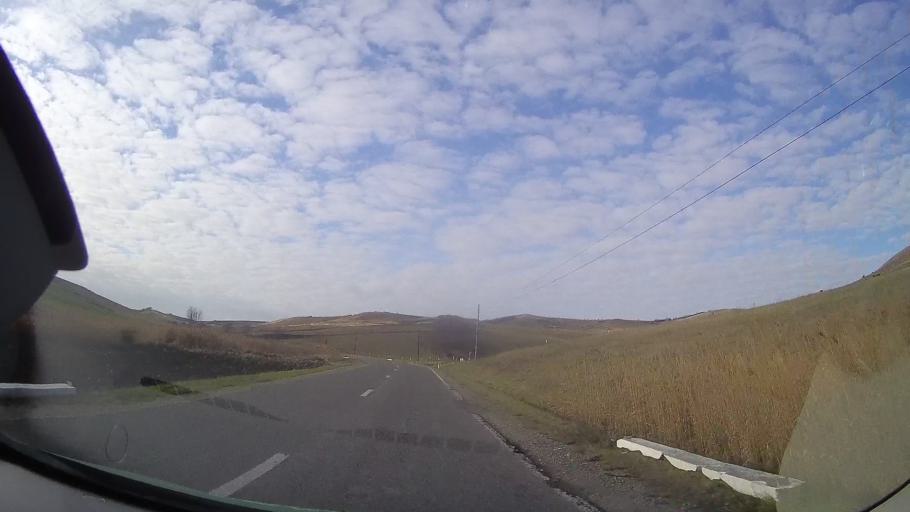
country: RO
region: Cluj
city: Jucu Herghelia
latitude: 46.8117
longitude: 23.8001
